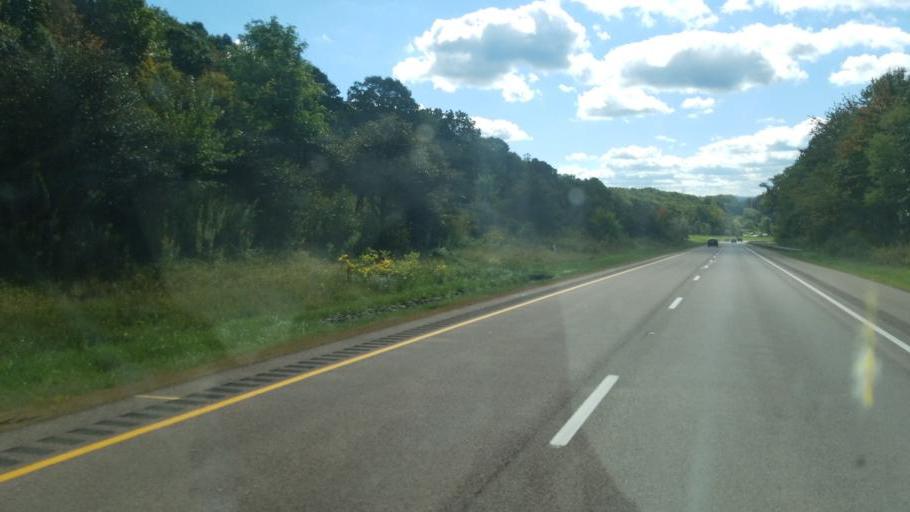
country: US
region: Maryland
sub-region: Garrett County
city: Oakland
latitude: 39.6820
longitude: -79.3662
